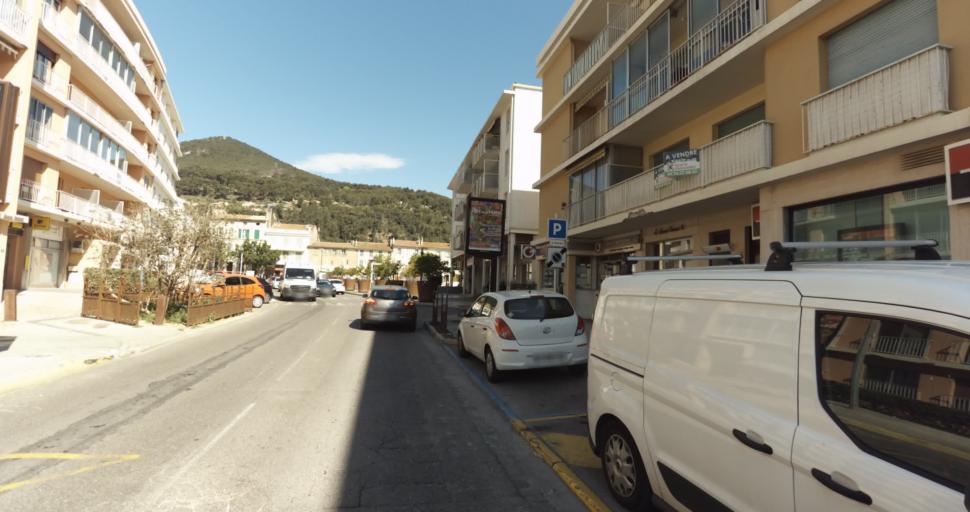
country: FR
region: Provence-Alpes-Cote d'Azur
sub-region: Departement du Var
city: La Valette-du-Var
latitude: 43.1364
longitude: 5.9816
